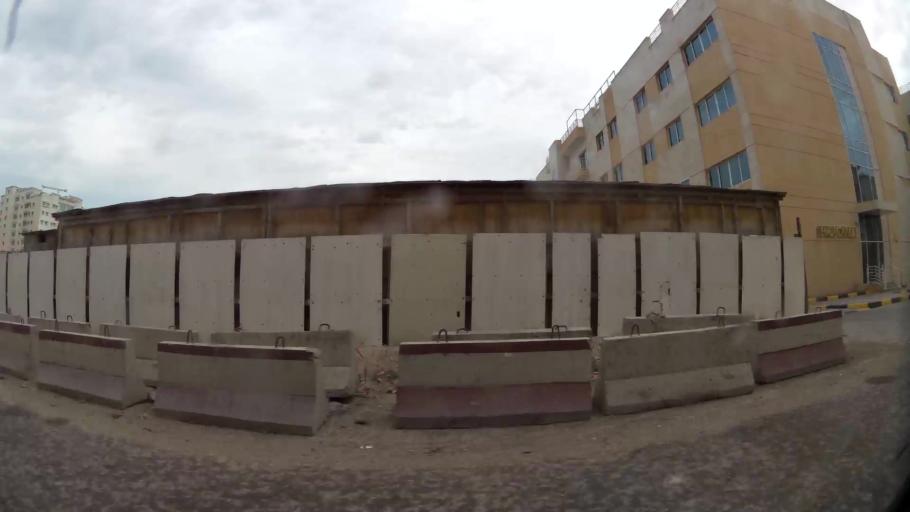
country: QA
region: Baladiyat ad Dawhah
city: Doha
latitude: 25.2779
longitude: 51.4964
